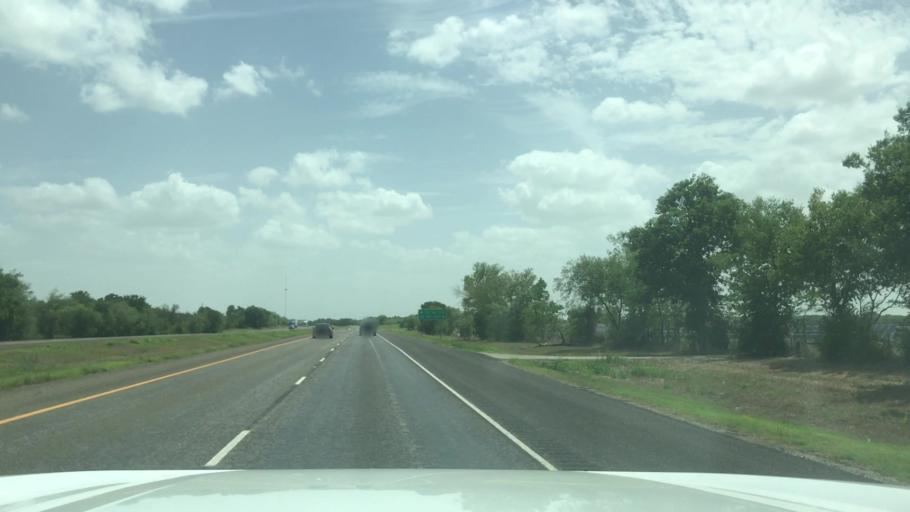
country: US
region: Texas
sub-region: Falls County
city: Marlin
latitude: 31.2883
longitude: -96.8752
